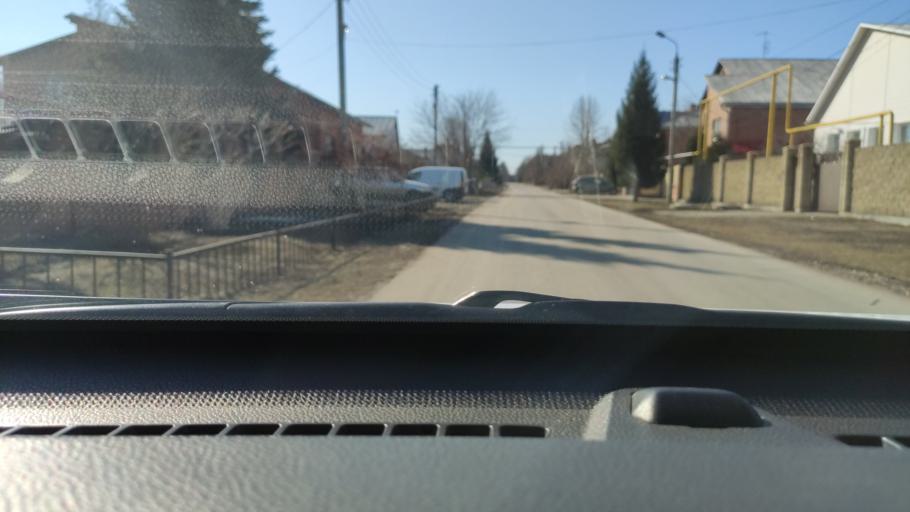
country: RU
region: Samara
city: Tol'yatti
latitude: 53.5644
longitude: 49.3877
